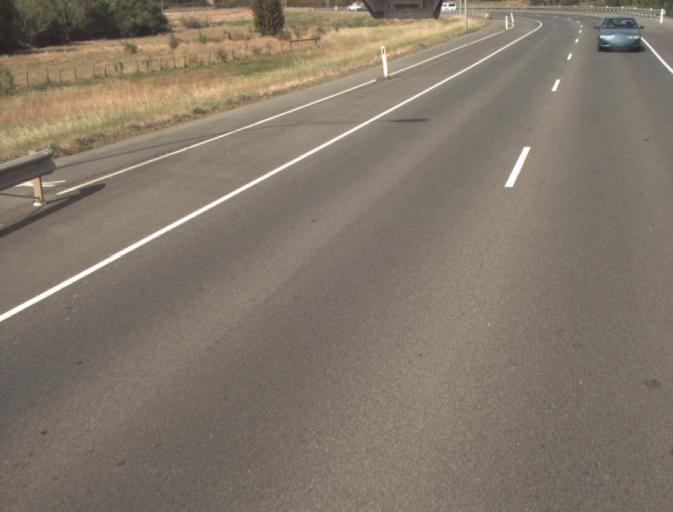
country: AU
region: Tasmania
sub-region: Launceston
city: Newstead
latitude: -41.4626
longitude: 147.1895
